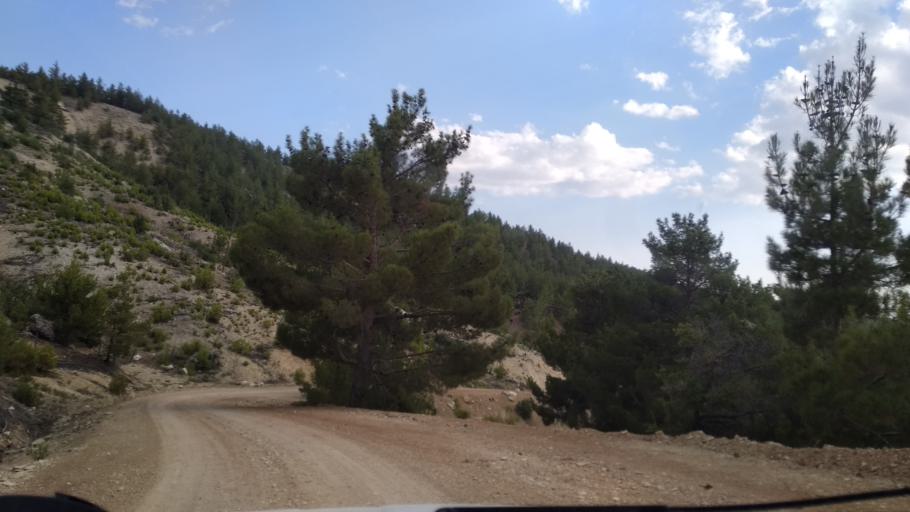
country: TR
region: Mersin
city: Sarikavak
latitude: 36.5966
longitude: 33.6860
